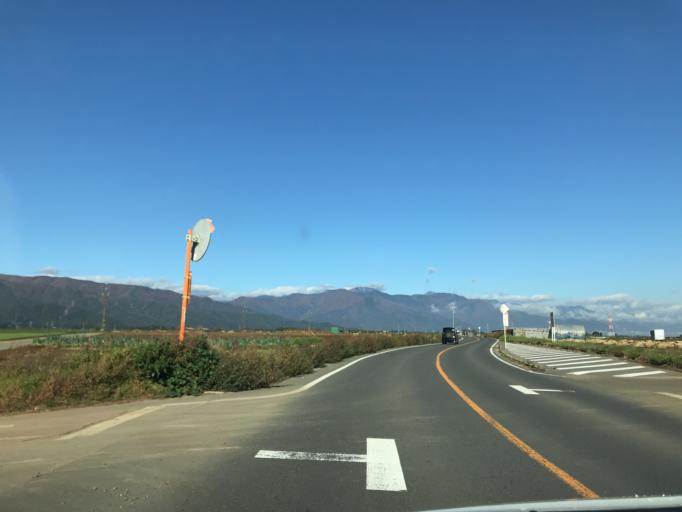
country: JP
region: Nagano
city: Shiojiri
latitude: 36.1335
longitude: 137.9225
